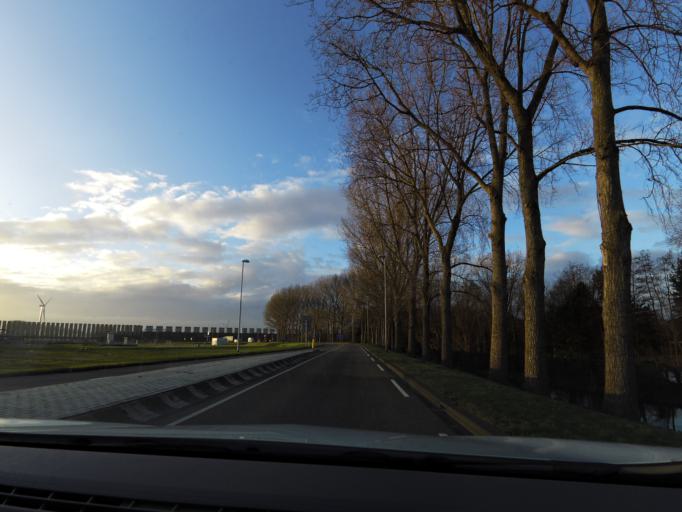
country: NL
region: South Holland
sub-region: Gemeente Maassluis
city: Maassluis
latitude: 51.9025
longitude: 4.2323
